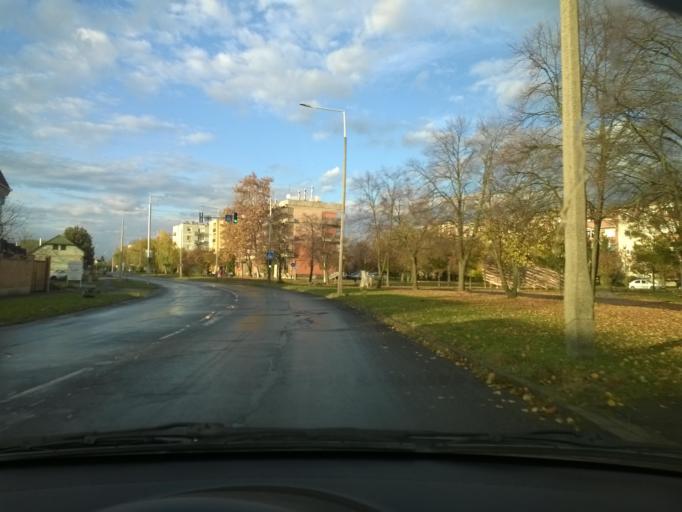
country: HU
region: Bacs-Kiskun
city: Kalocsa
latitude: 46.5311
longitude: 18.9869
